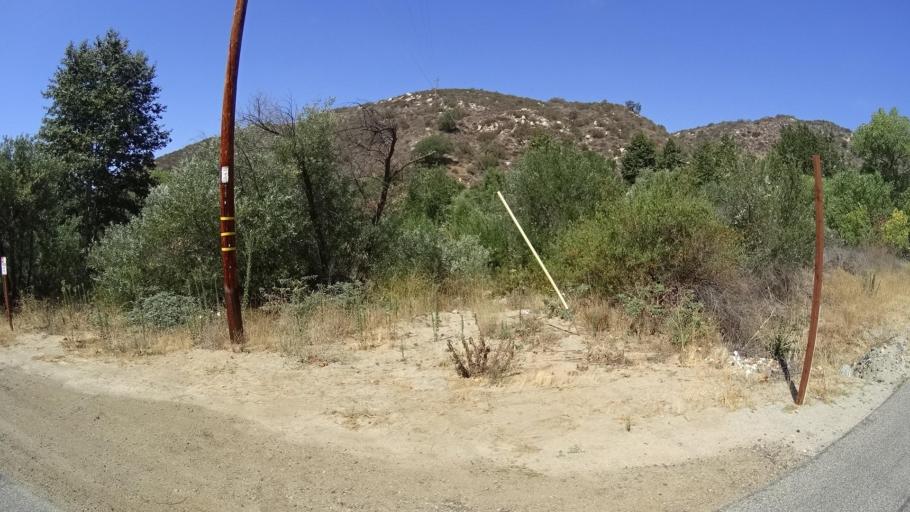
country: US
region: California
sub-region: San Diego County
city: Fallbrook
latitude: 33.4062
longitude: -117.2492
